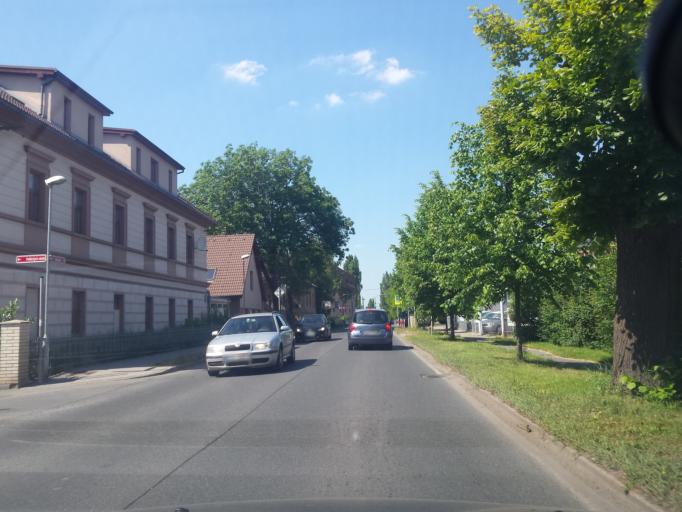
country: CZ
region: Central Bohemia
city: Horomerice
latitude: 50.1360
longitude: 14.3364
